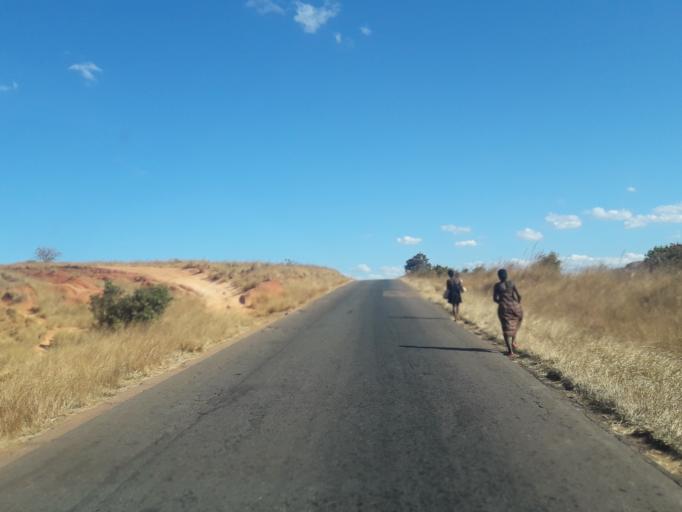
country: MG
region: Analamanga
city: Ankazobe
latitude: -17.6654
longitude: 46.9847
